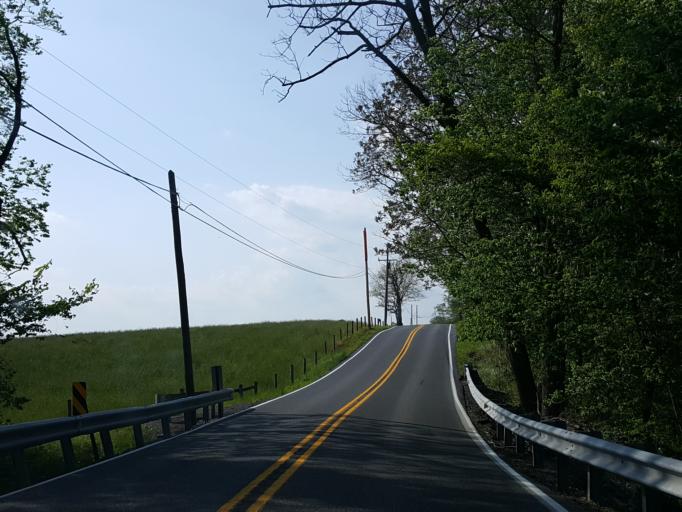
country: US
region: Pennsylvania
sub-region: Lebanon County
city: Campbelltown
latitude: 40.2491
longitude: -76.6054
